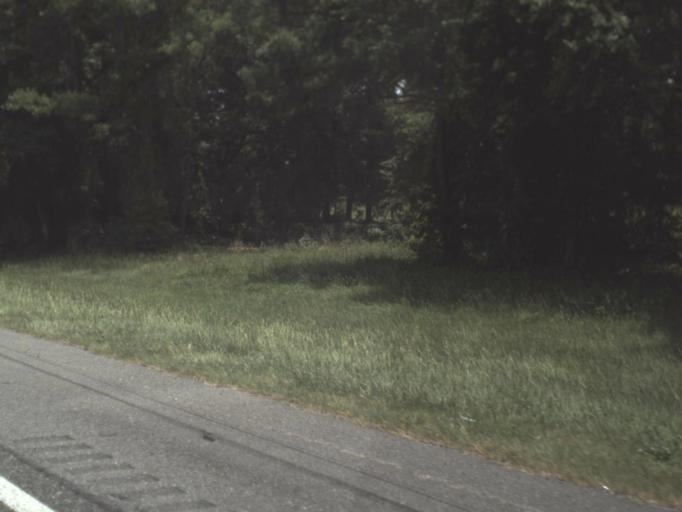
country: US
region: Florida
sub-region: Columbia County
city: Lake City
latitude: 30.0748
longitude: -82.6314
